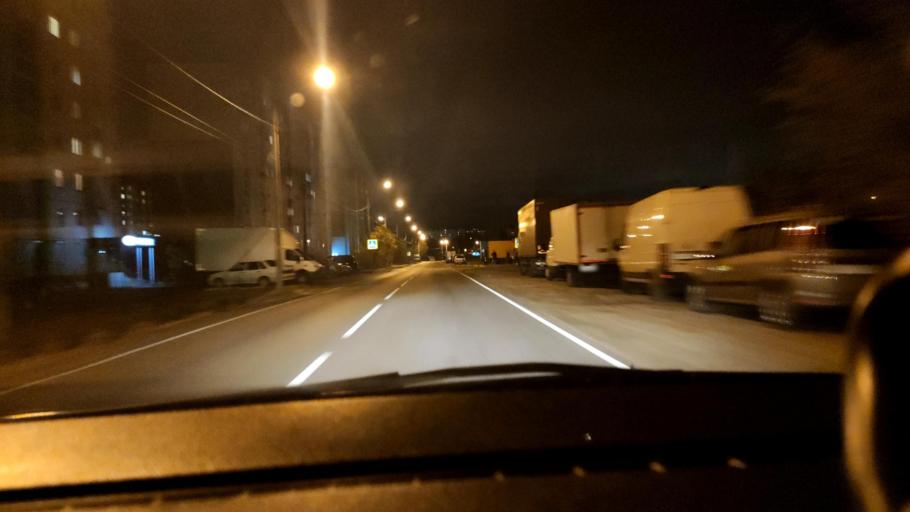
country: RU
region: Voronezj
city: Pridonskoy
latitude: 51.6193
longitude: 39.0637
